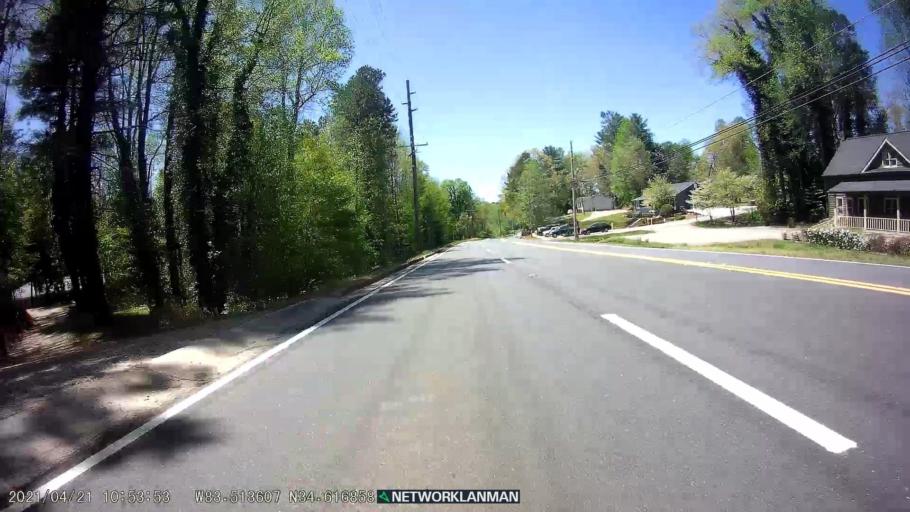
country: US
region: Georgia
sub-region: Habersham County
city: Clarkesville
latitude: 34.6169
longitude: -83.5134
